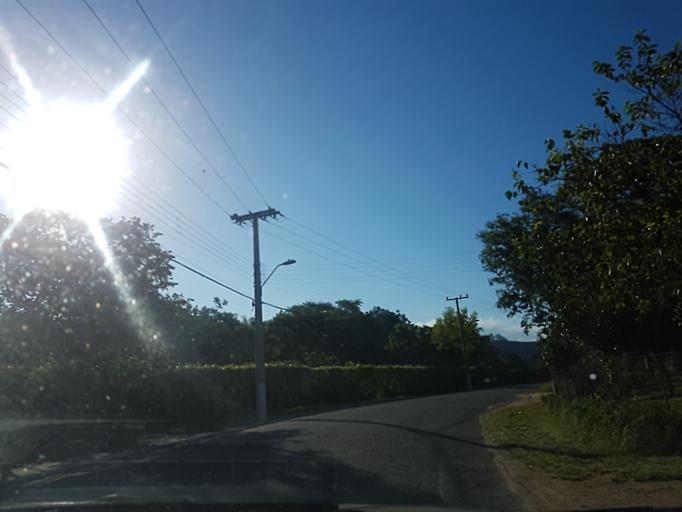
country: BR
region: Santa Catarina
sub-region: Braco Do Norte
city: Braco do Norte
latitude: -28.3303
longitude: -49.1721
